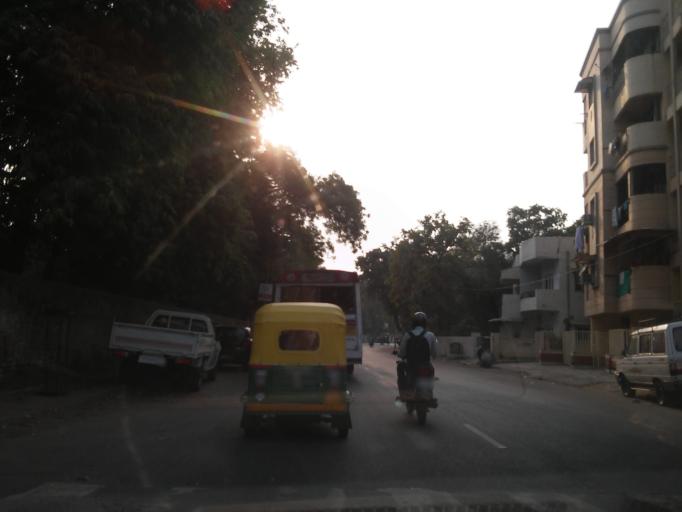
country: IN
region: Gujarat
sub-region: Ahmadabad
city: Ahmedabad
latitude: 23.0099
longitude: 72.5521
